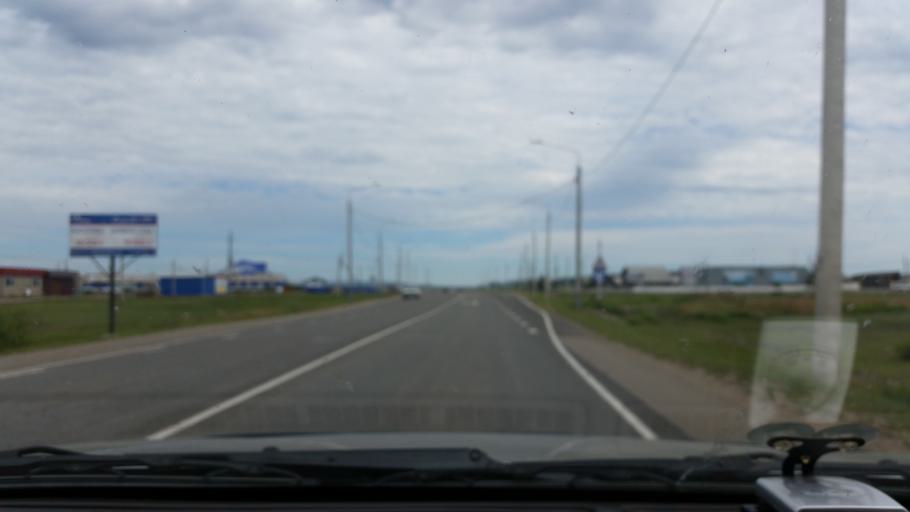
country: RU
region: Irkutsk
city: Bayanday
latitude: 53.0519
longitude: 105.5229
